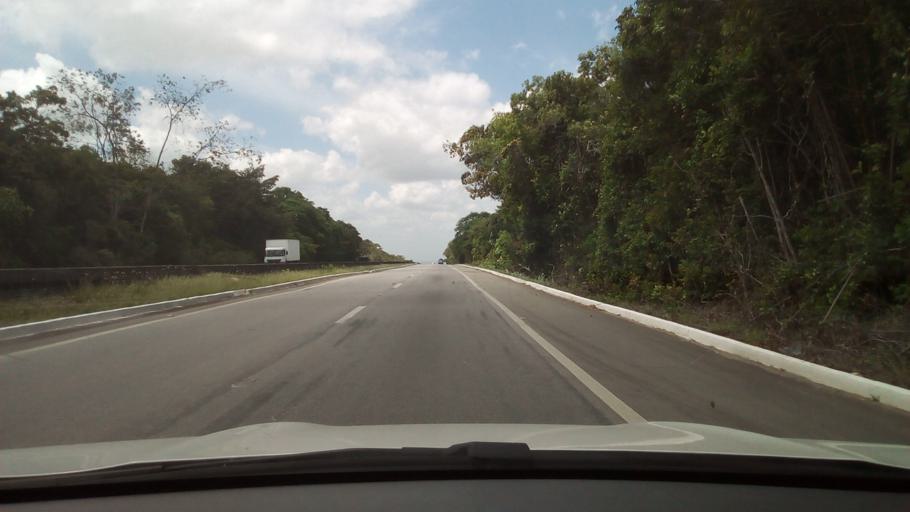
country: BR
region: Paraiba
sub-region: Mamanguape
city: Mamanguape
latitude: -6.9723
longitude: -35.0807
